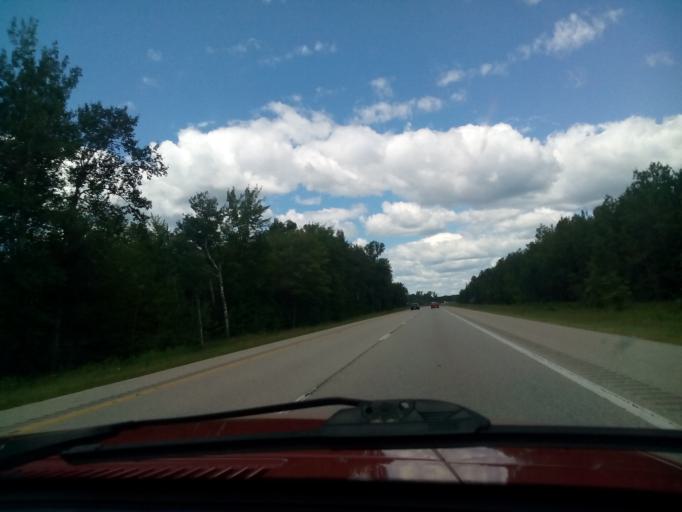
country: US
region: Michigan
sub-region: Ogemaw County
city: Skidway Lake
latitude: 44.0773
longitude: -84.0956
